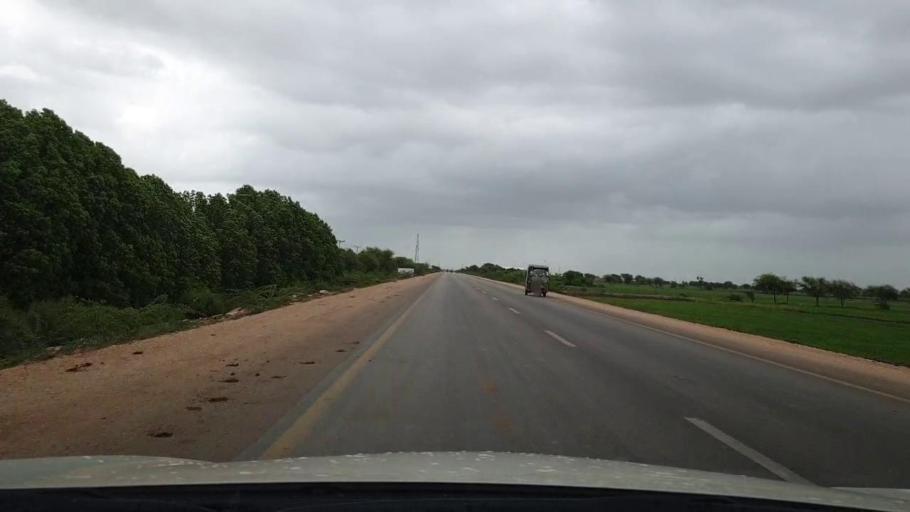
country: PK
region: Sindh
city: Badin
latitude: 24.6555
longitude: 68.7368
